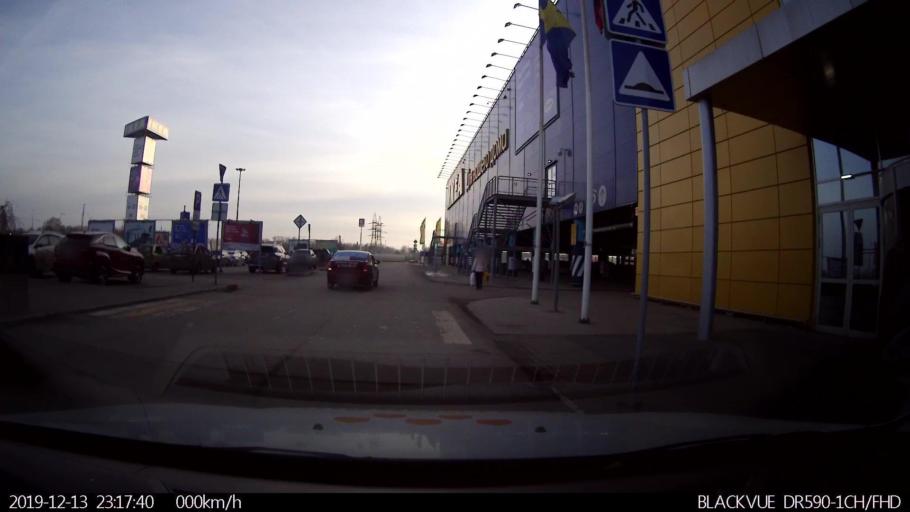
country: RU
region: Nizjnij Novgorod
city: Afonino
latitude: 56.2248
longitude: 44.0738
